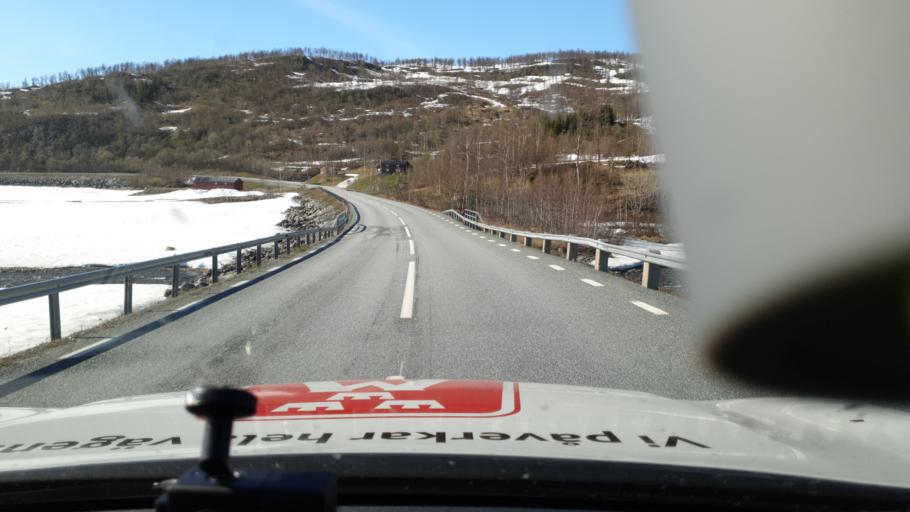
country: NO
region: Nordland
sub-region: Rana
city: Mo i Rana
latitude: 66.0991
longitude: 14.8497
